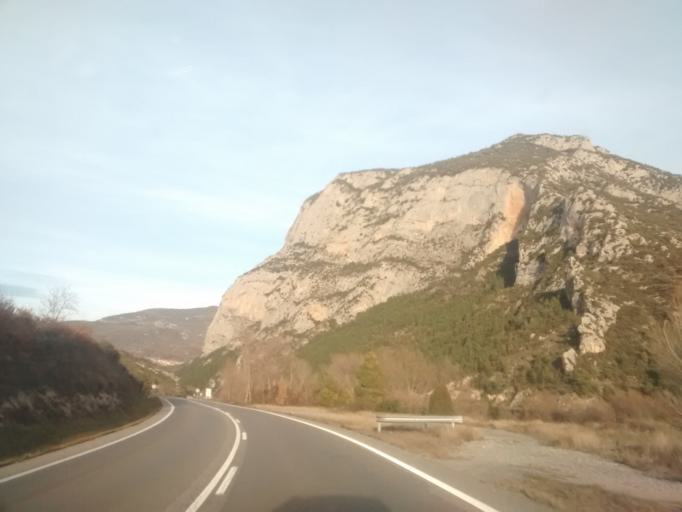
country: ES
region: Catalonia
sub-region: Provincia de Lleida
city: Coll de Nargo
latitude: 42.1820
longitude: 1.3260
